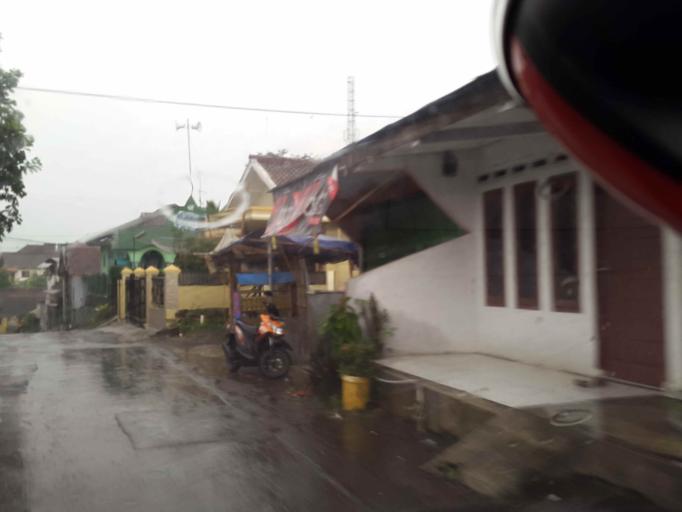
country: ID
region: West Java
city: Sukabumi
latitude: -6.9019
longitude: 106.9282
